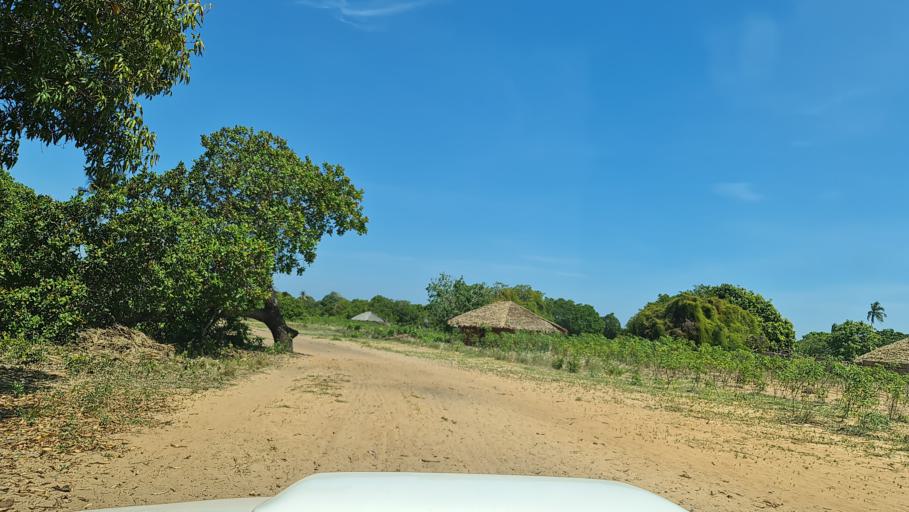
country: MZ
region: Nampula
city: Ilha de Mocambique
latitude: -15.1979
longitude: 40.6056
